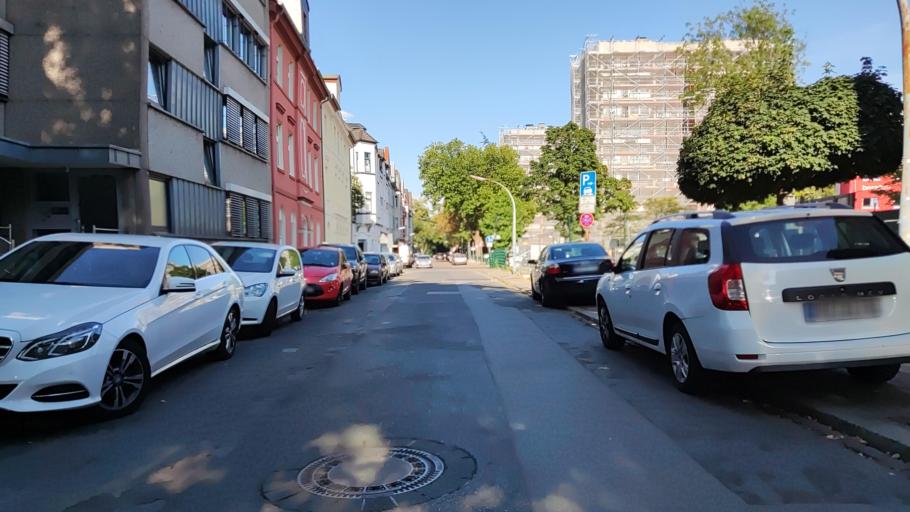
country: DE
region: North Rhine-Westphalia
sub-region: Regierungsbezirk Arnsberg
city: Herne
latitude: 51.5392
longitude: 7.2257
